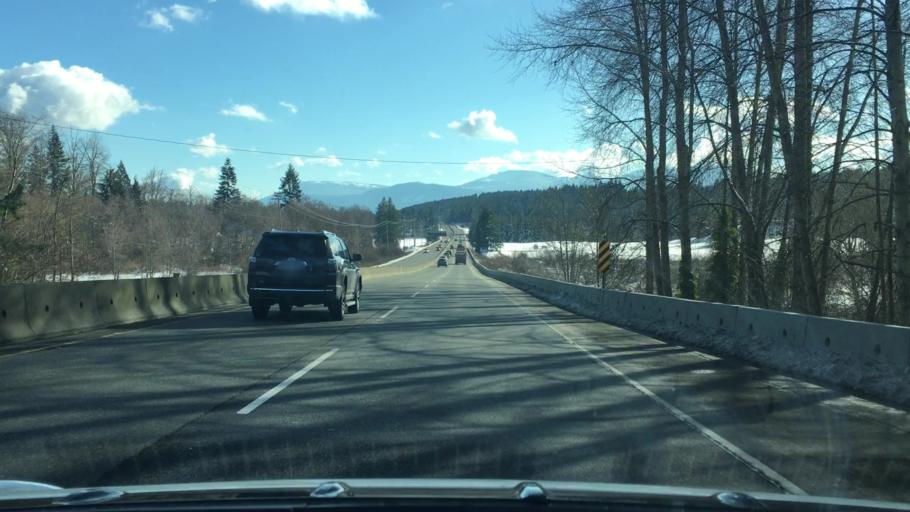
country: CA
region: British Columbia
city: Nanaimo
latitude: 49.0859
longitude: -123.8832
